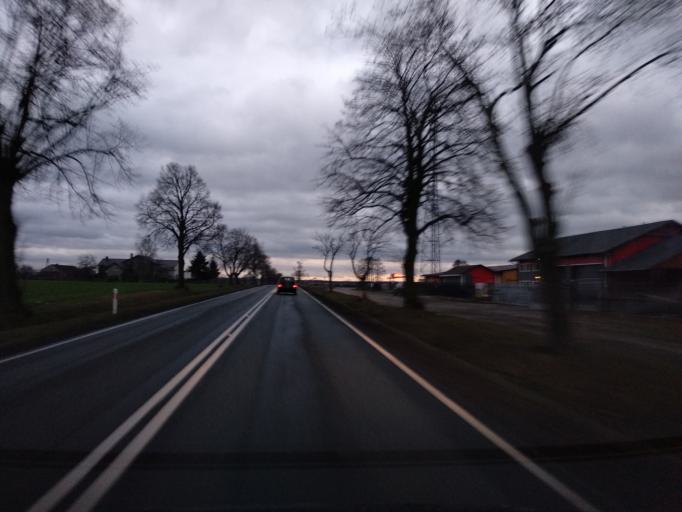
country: PL
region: Greater Poland Voivodeship
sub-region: Powiat koninski
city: Rychwal
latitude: 52.0555
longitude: 18.1632
